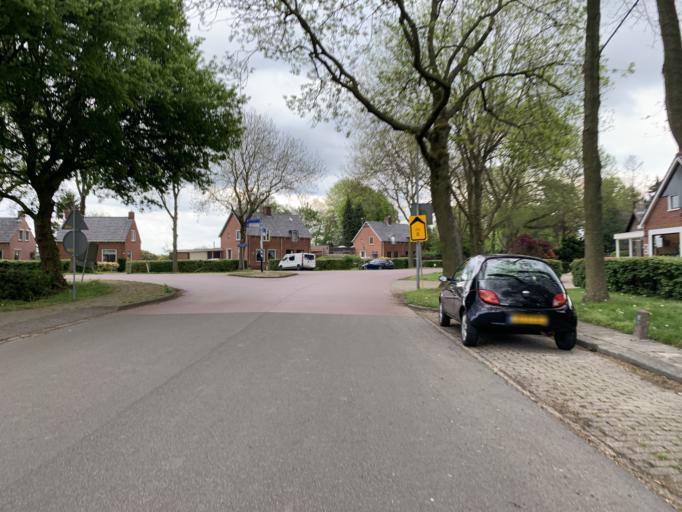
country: NL
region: Groningen
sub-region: Gemeente Haren
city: Haren
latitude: 53.2147
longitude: 6.6405
